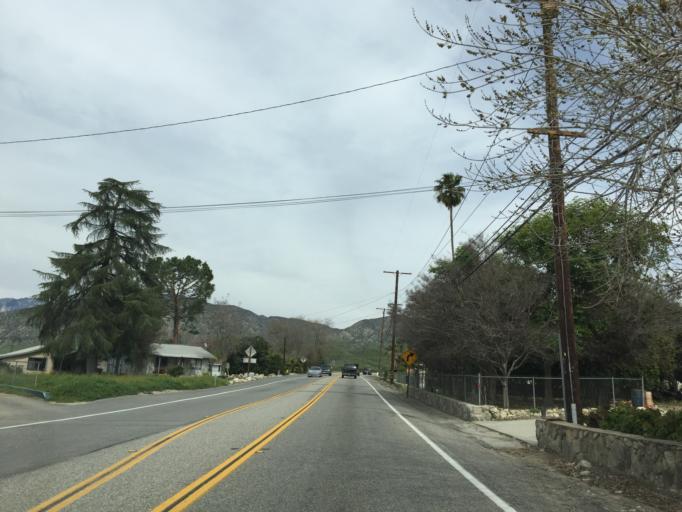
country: US
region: California
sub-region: San Bernardino County
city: Mentone
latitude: 34.0718
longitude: -117.0988
